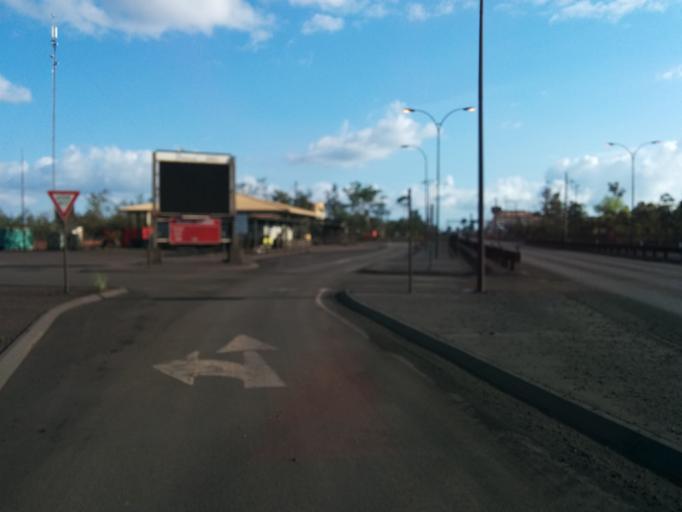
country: AU
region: Northern Territory
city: Alyangula
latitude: -13.9754
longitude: 136.4428
